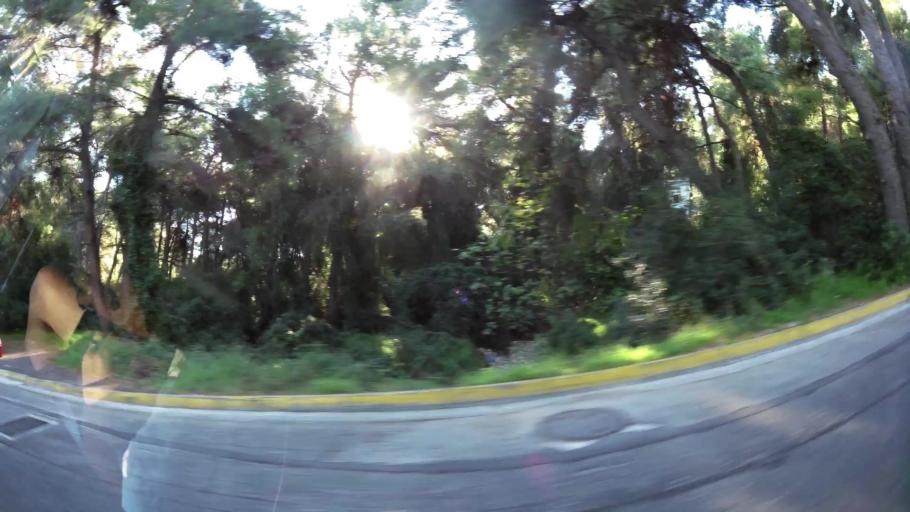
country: GR
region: Attica
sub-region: Nomarchia Anatolikis Attikis
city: Drosia
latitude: 38.1169
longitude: 23.8548
